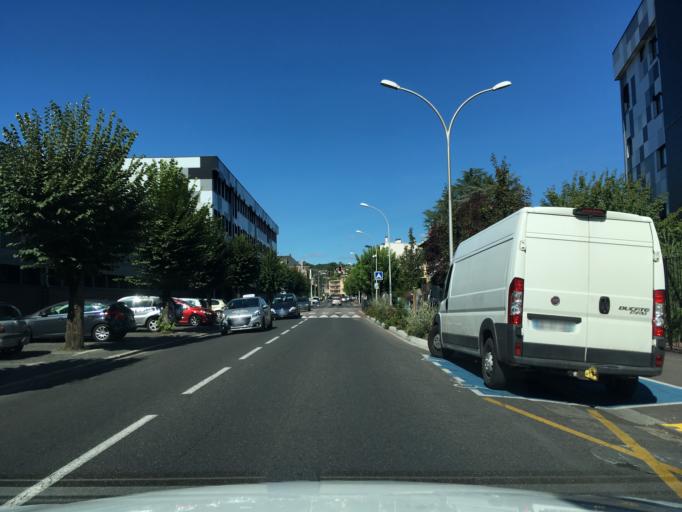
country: FR
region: Limousin
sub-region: Departement de la Correze
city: Brive-la-Gaillarde
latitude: 45.1595
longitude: 1.5234
